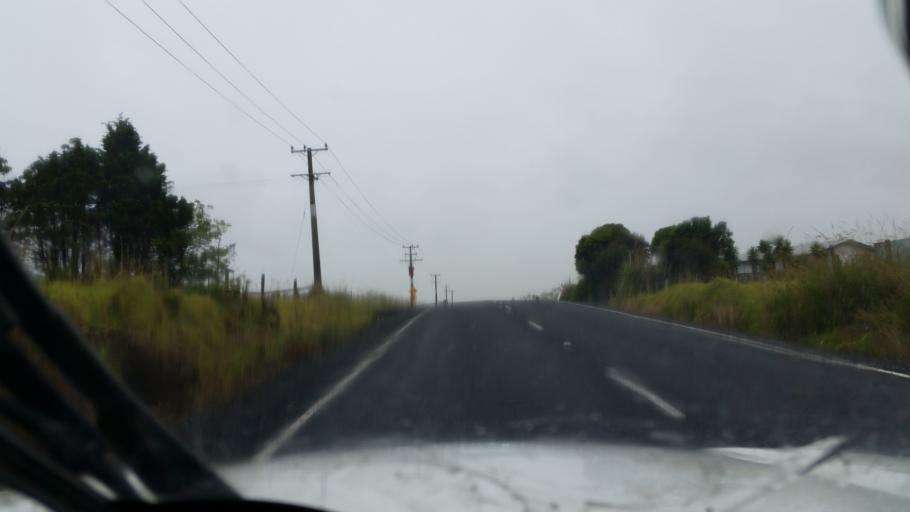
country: NZ
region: Northland
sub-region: Far North District
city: Ahipara
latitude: -35.1811
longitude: 173.1681
